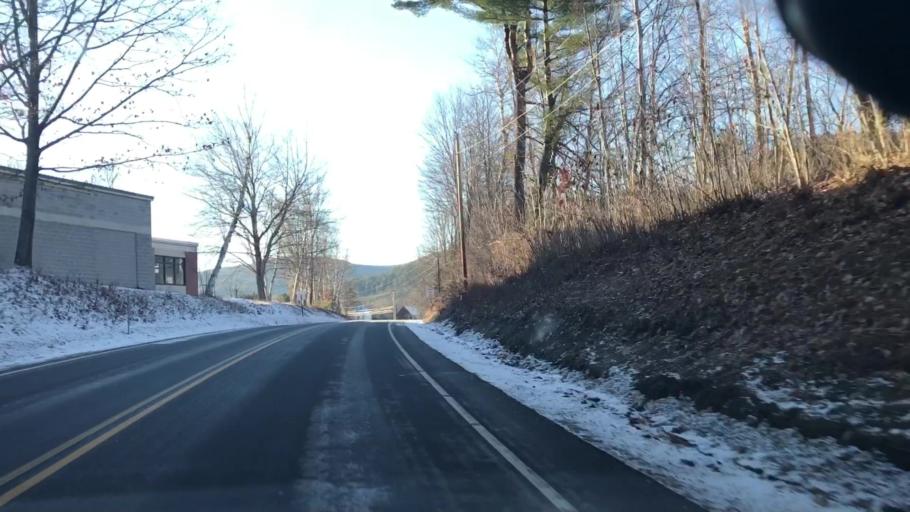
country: US
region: New Hampshire
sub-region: Grafton County
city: Orford
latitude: 43.9092
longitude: -72.1286
